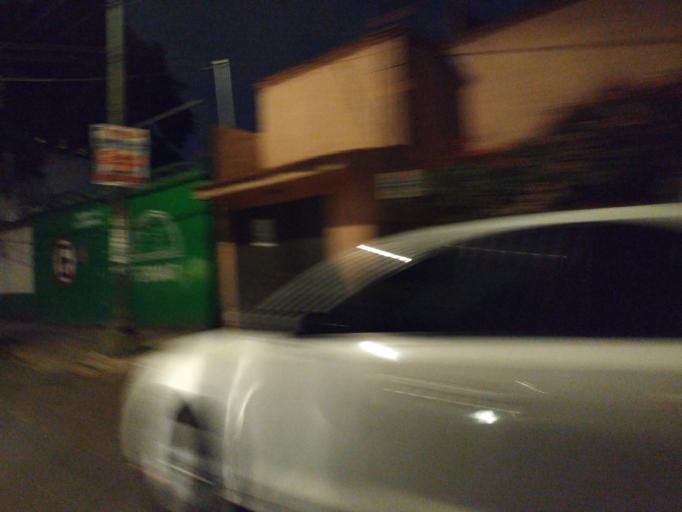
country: MX
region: Mexico City
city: Coyoacan
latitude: 19.3499
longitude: -99.1504
